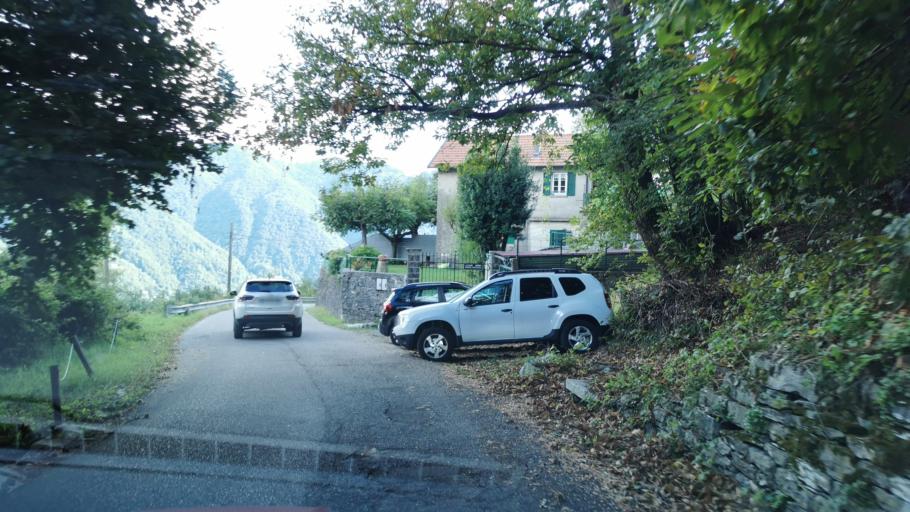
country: IT
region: Lombardy
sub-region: Provincia di Como
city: Moltrasio
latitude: 45.8566
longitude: 9.0862
